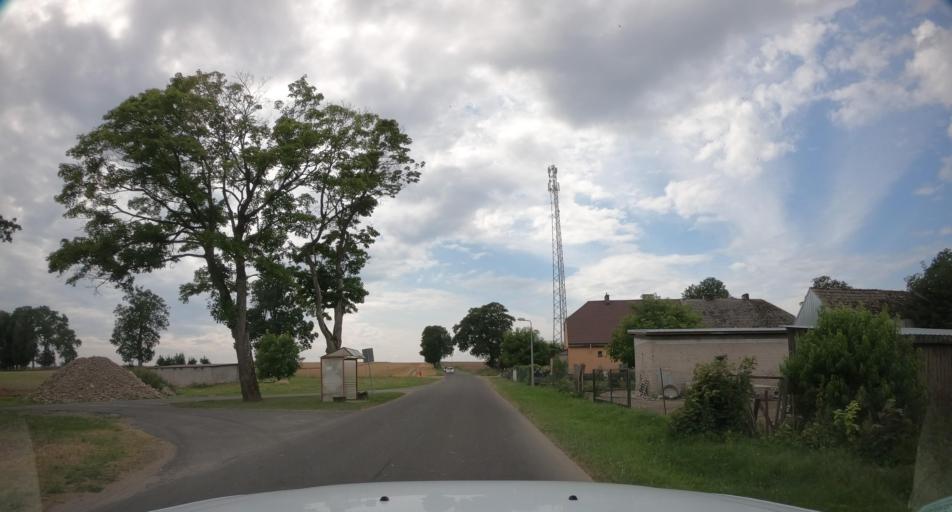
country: PL
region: West Pomeranian Voivodeship
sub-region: Powiat walecki
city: Walcz
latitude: 53.2336
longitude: 16.3146
